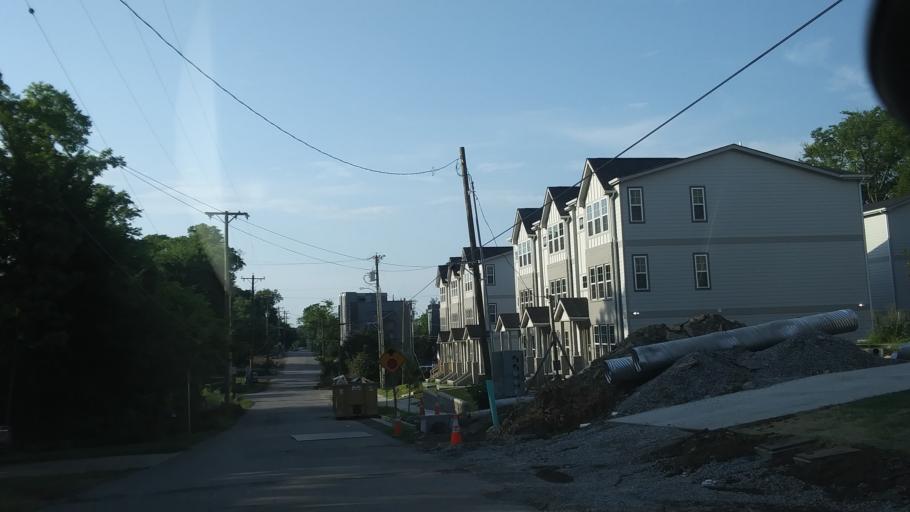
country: US
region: Tennessee
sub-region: Davidson County
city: Belle Meade
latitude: 36.1439
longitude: -86.8595
